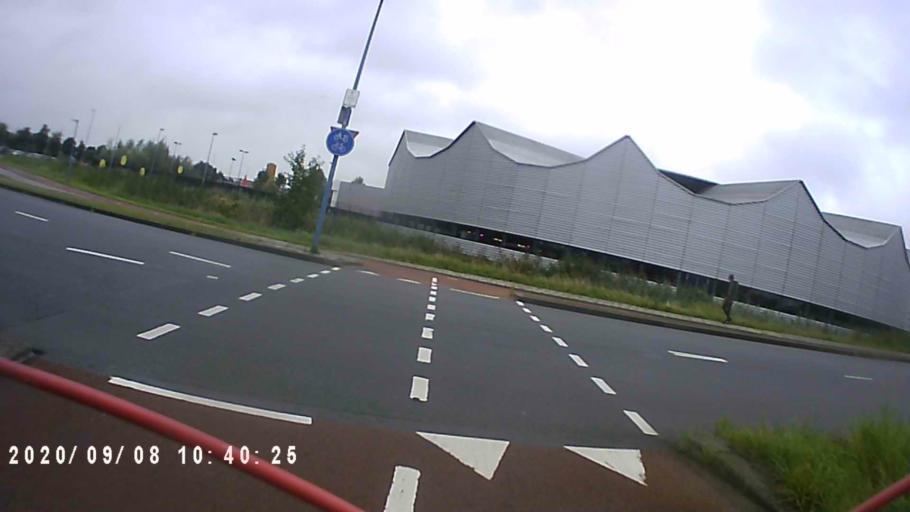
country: NL
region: Groningen
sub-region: Gemeente Groningen
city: Oosterpark
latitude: 53.2377
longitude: 6.5942
